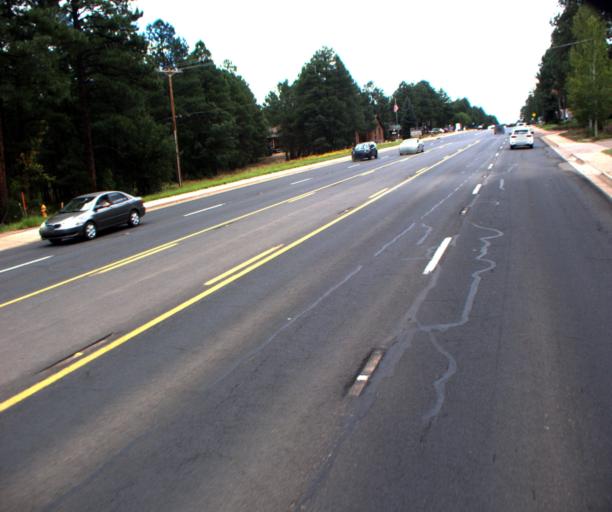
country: US
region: Arizona
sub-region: Navajo County
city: Pinetop-Lakeside
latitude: 34.1371
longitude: -109.9512
